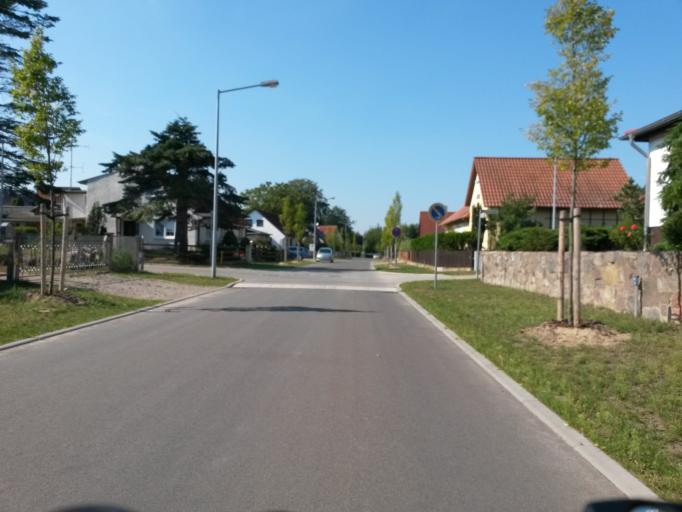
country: DE
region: Brandenburg
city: Templin
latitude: 53.1114
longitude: 13.4840
